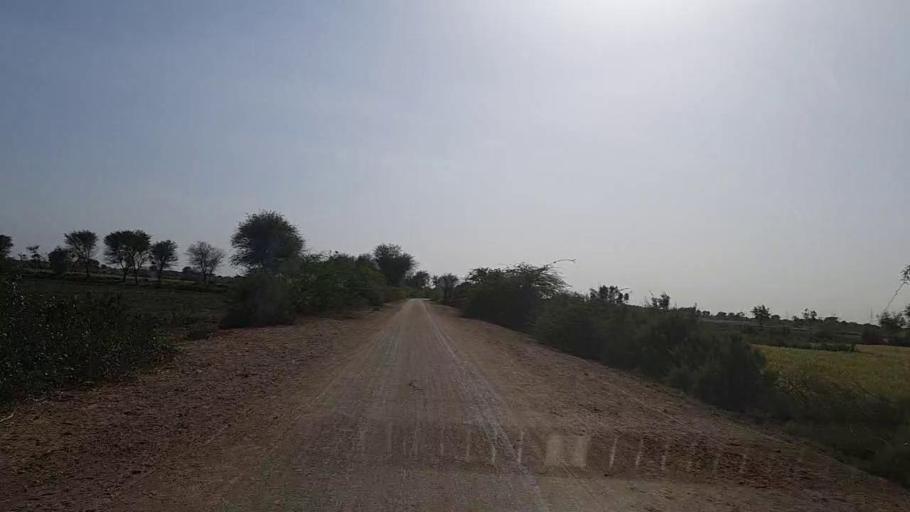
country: PK
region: Sindh
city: Kotri
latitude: 25.1575
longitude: 68.2928
